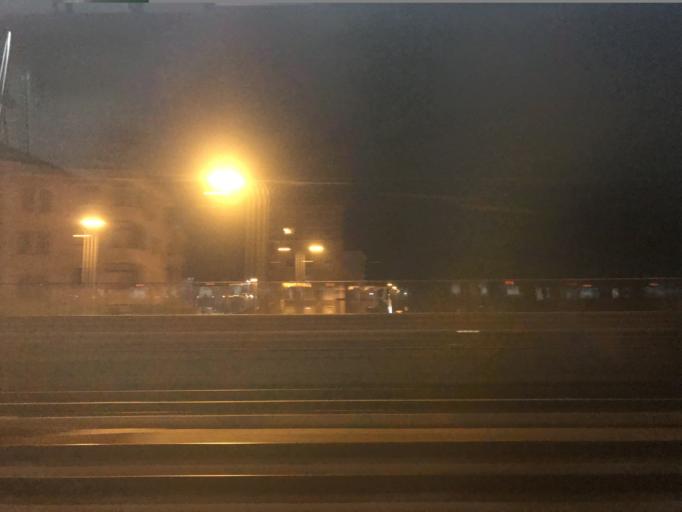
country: TR
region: Istanbul
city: Pendik
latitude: 40.8808
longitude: 29.2216
